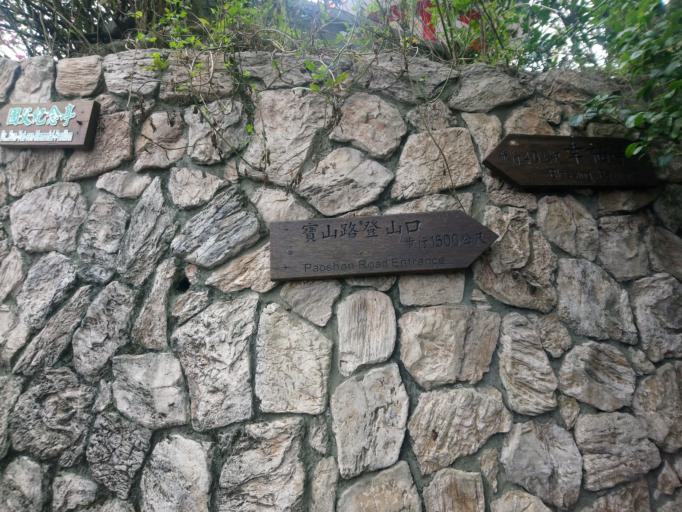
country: TW
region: Taiwan
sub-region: Hsinchu
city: Hsinchu
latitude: 24.7931
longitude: 120.9853
